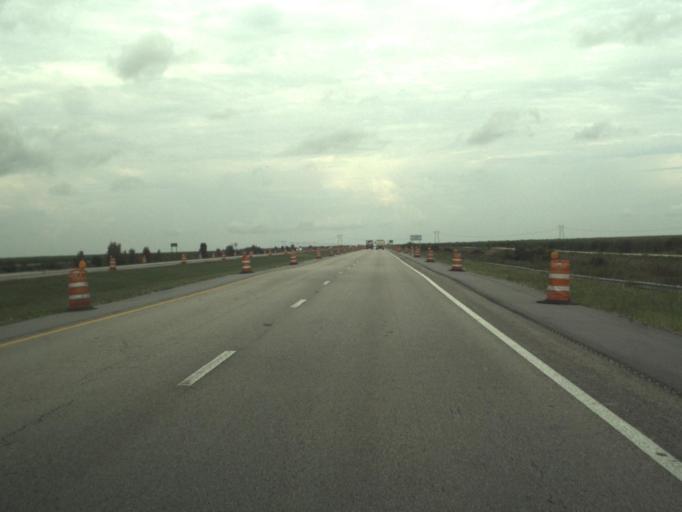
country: US
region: Florida
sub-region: Palm Beach County
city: Loxahatchee Groves
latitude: 26.6914
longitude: -80.3945
